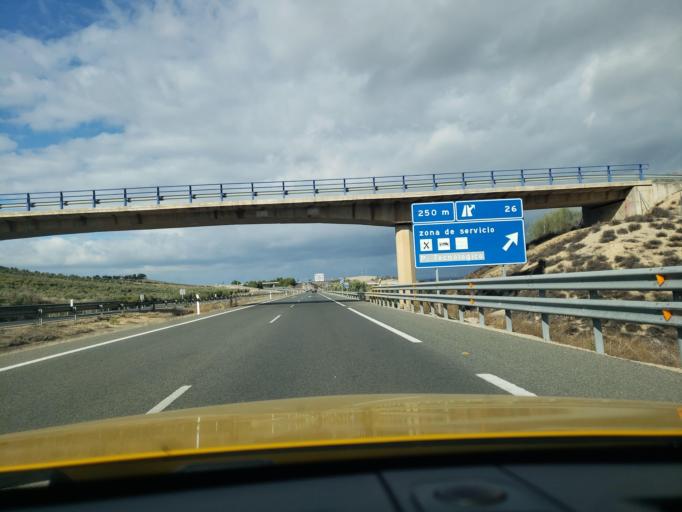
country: ES
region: Andalusia
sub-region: Provincia de Jaen
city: Mengibar
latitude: 37.9017
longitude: -3.7815
